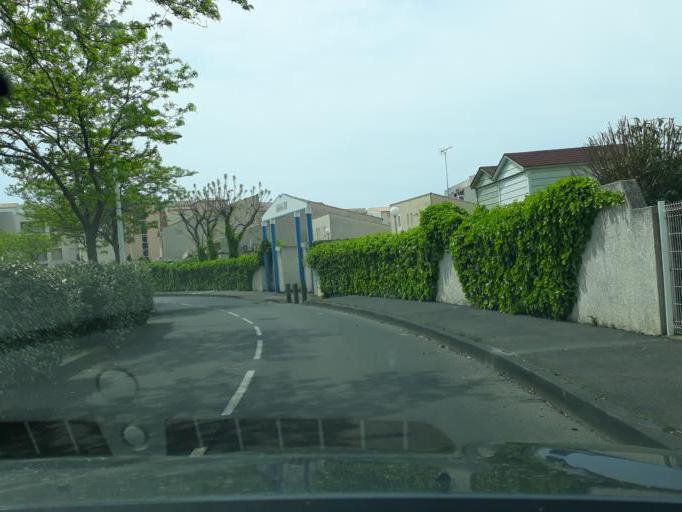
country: FR
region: Languedoc-Roussillon
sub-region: Departement de l'Herault
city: Le Cap d'Agde
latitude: 43.2766
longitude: 3.4831
